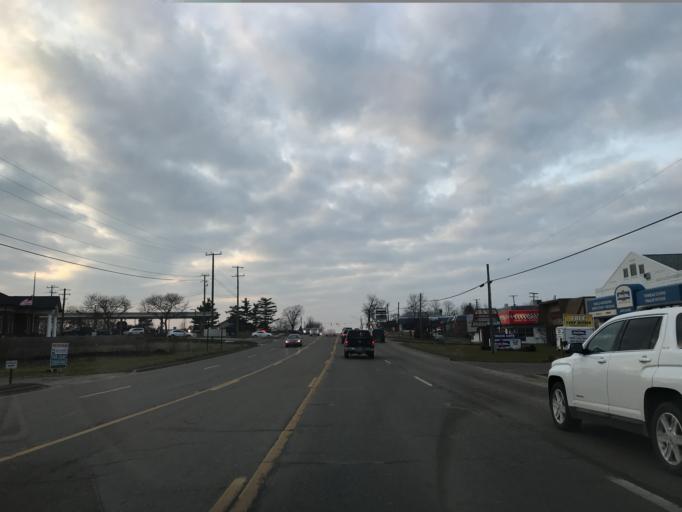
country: US
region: Michigan
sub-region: Livingston County
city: Brighton
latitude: 42.5213
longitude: -83.7602
